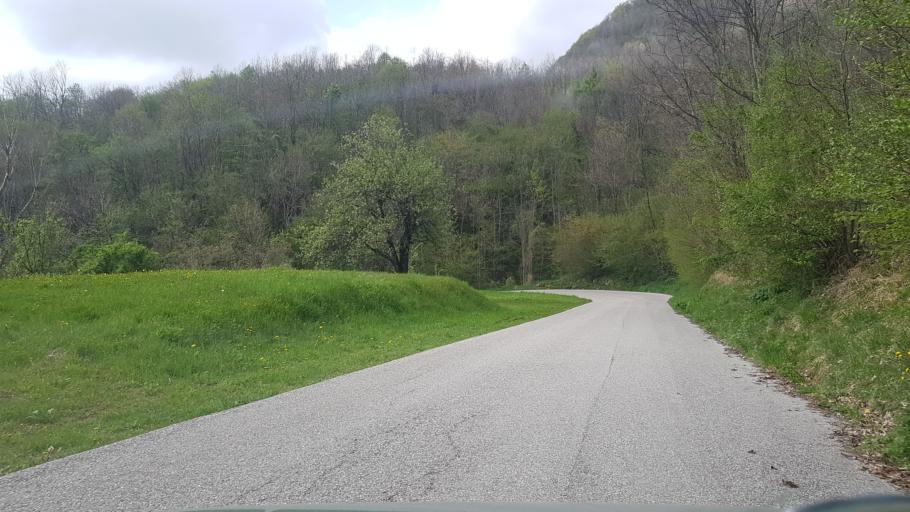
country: IT
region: Friuli Venezia Giulia
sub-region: Provincia di Udine
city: Attimis
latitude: 46.2051
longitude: 13.3513
